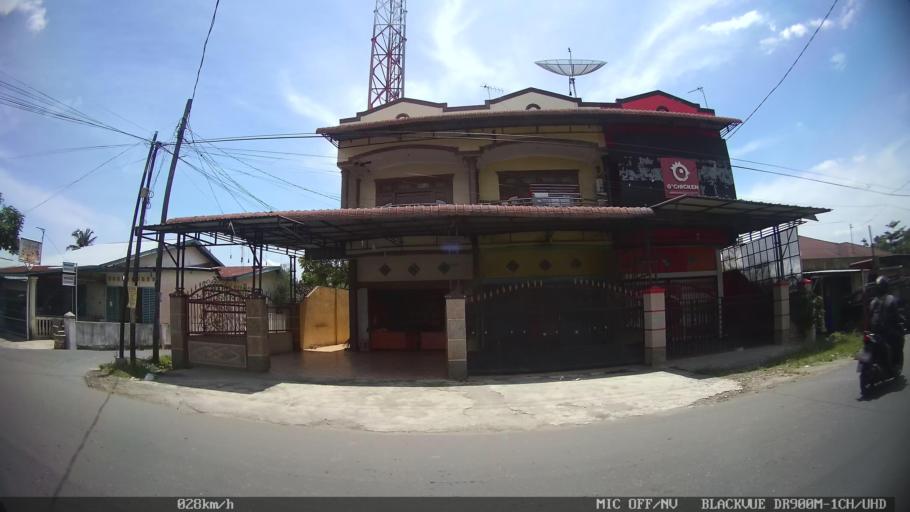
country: ID
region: North Sumatra
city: Binjai
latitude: 3.6019
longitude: 98.4962
